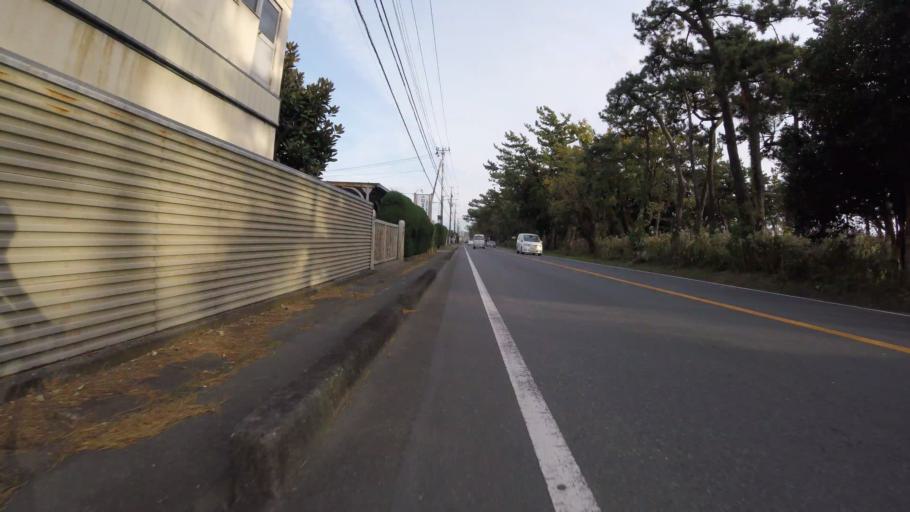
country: JP
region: Shizuoka
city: Fuji
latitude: 35.1293
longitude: 138.7734
